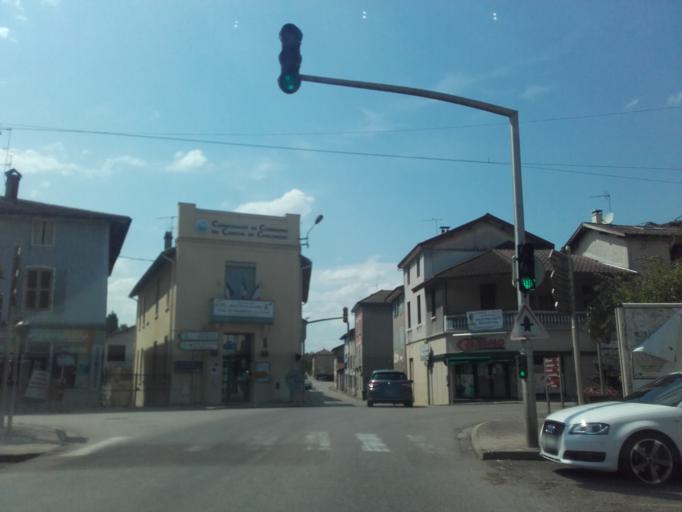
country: FR
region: Rhone-Alpes
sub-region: Departement de l'Ain
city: Chalamont
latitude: 45.9970
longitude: 5.1711
